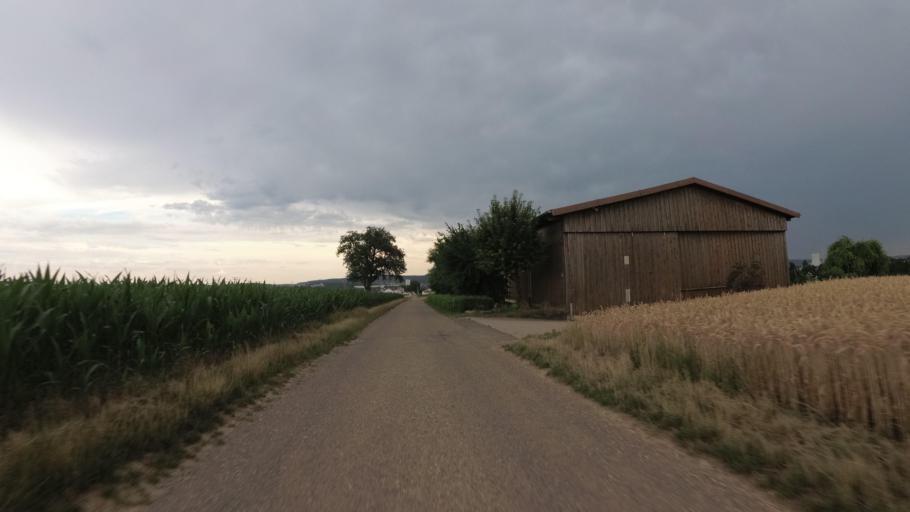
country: DE
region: Baden-Wuerttemberg
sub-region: Regierungsbezirk Stuttgart
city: Untereisesheim
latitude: 49.2132
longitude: 9.1890
